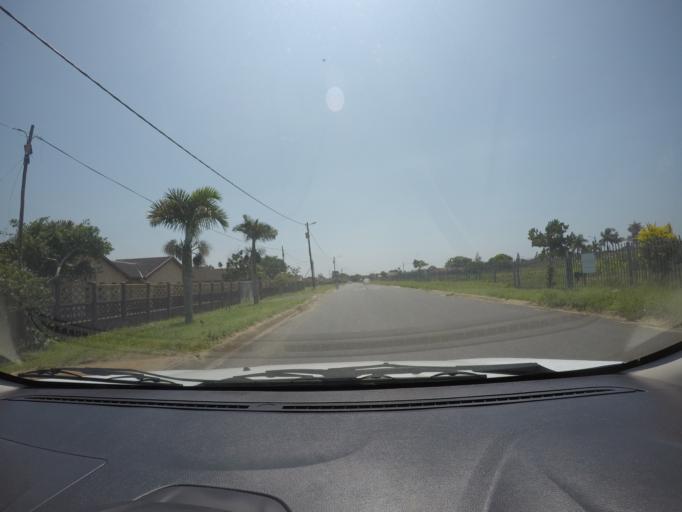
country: ZA
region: KwaZulu-Natal
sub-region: uThungulu District Municipality
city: eSikhawini
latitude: -28.8651
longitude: 31.9230
